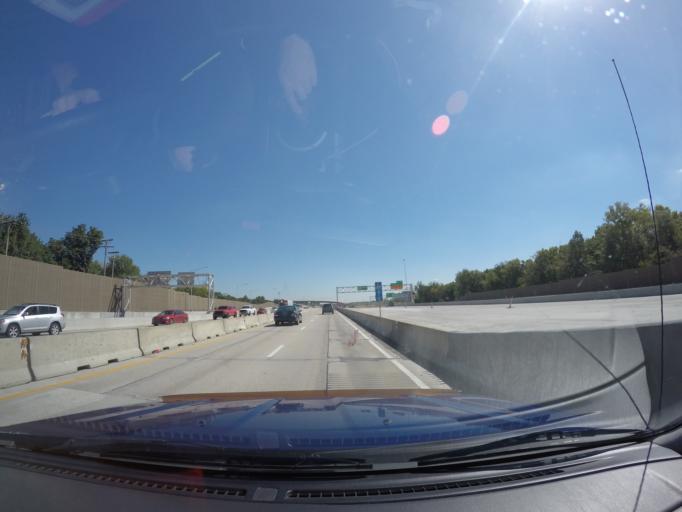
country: US
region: Kansas
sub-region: Johnson County
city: Lenexa
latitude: 38.9352
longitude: -94.7142
